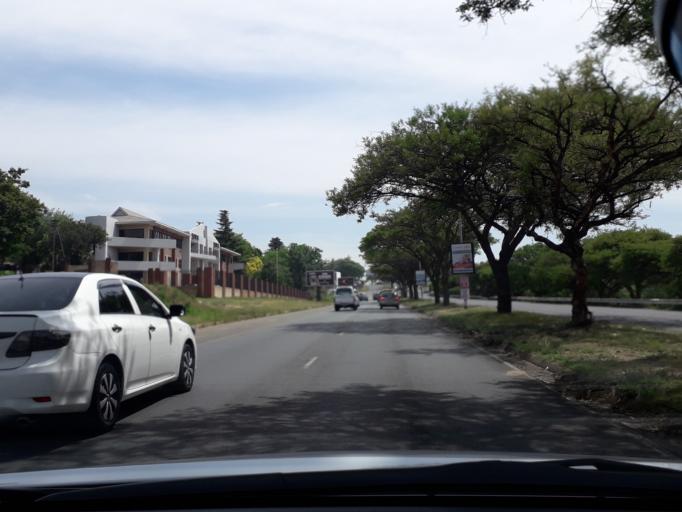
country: ZA
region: Gauteng
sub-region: City of Johannesburg Metropolitan Municipality
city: Johannesburg
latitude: -26.0787
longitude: 28.0256
